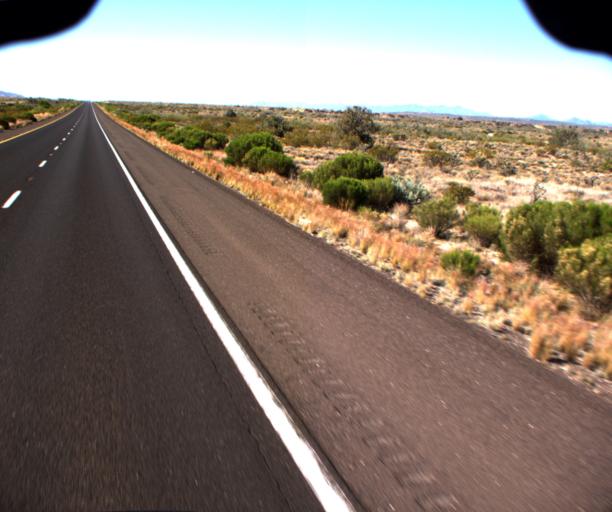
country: US
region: Arizona
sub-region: Mohave County
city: New Kingman-Butler
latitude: 35.1249
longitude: -113.6670
